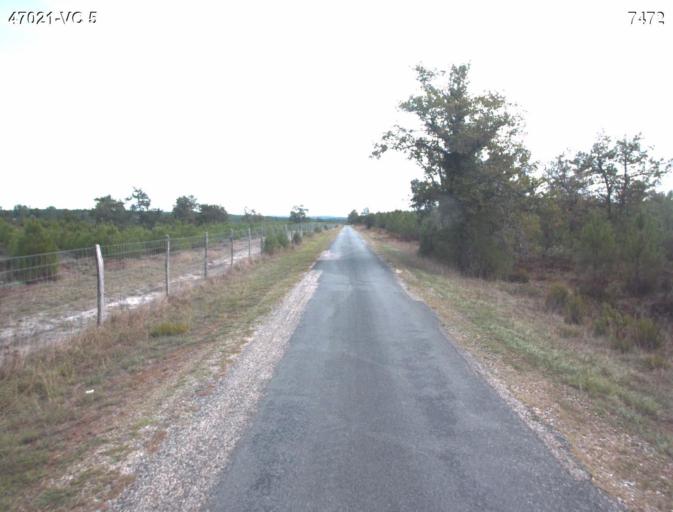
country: FR
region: Aquitaine
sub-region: Departement du Lot-et-Garonne
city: Barbaste
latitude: 44.1520
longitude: 0.2083
